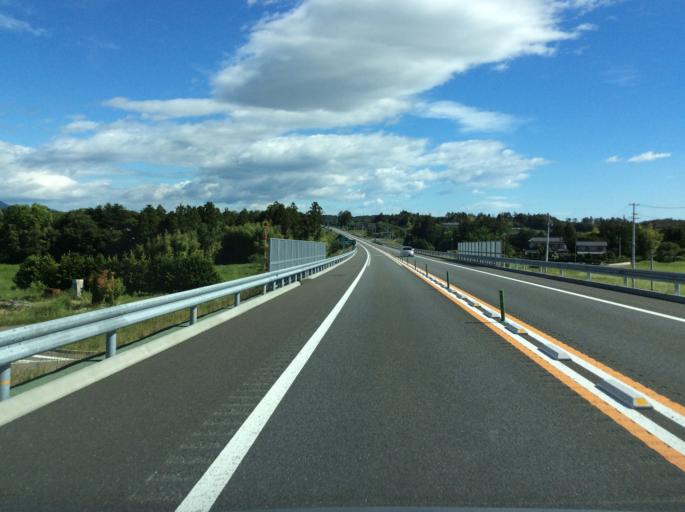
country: JP
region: Fukushima
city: Namie
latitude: 37.5563
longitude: 140.9452
